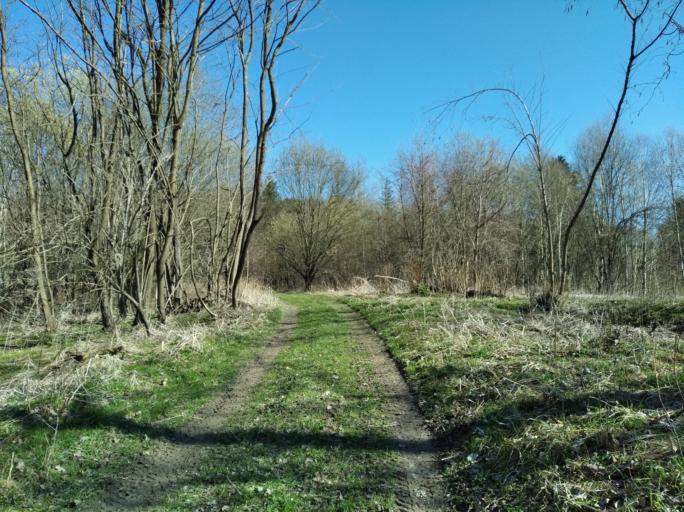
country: PL
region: Subcarpathian Voivodeship
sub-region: Powiat strzyzowski
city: Jawornik
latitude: 49.8346
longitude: 21.8509
